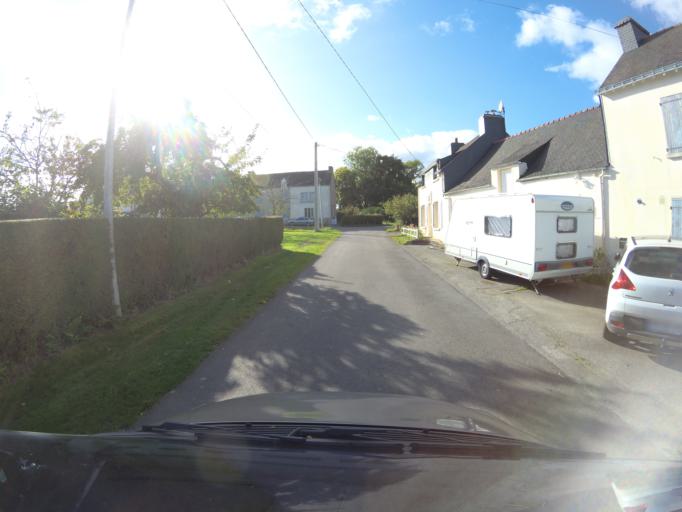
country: FR
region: Brittany
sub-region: Departement du Morbihan
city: Peillac
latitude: 47.7206
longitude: -2.2232
